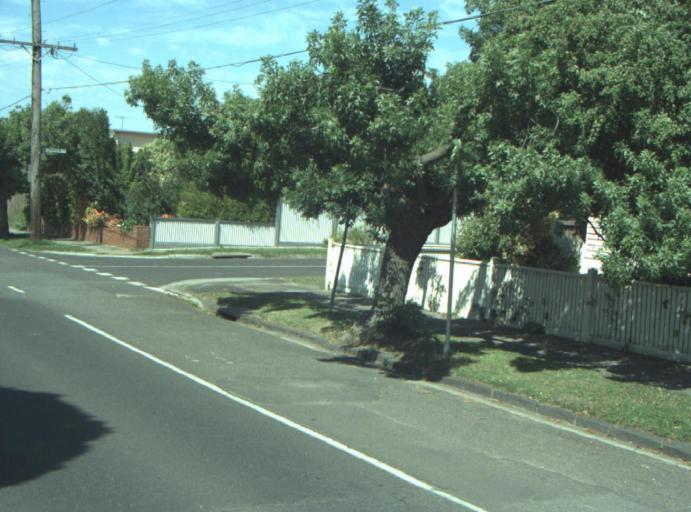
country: AU
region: Victoria
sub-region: Greater Geelong
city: Geelong West
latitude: -38.1421
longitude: 144.3296
